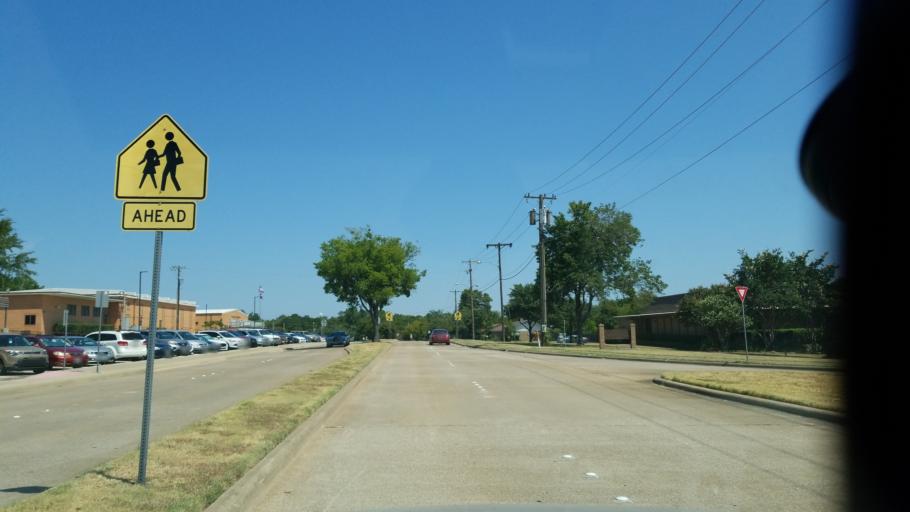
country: US
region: Texas
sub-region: Dallas County
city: Duncanville
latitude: 32.6478
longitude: -96.9000
